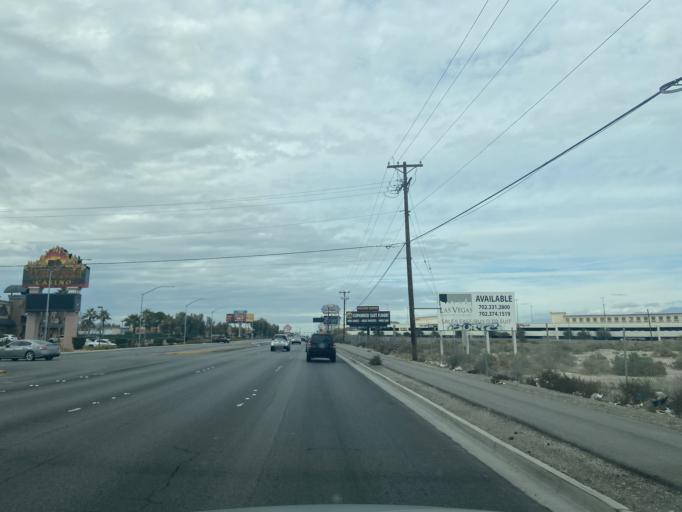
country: US
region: Nevada
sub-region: Clark County
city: Las Vegas
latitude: 36.1936
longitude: -115.1905
